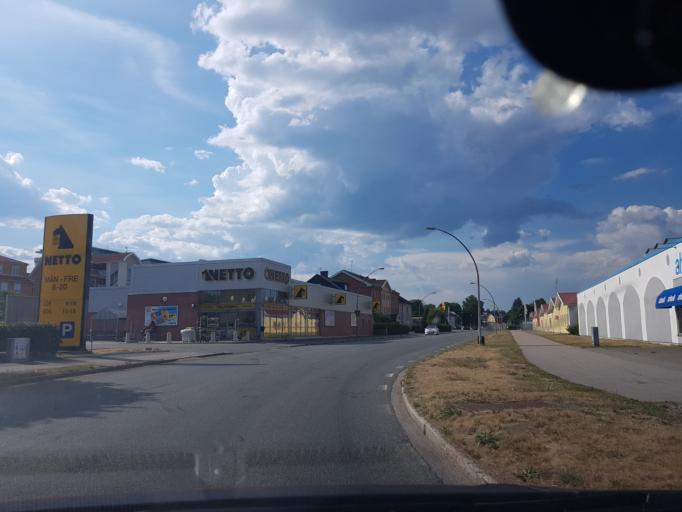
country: SE
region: Joenkoeping
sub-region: Gislaveds Kommun
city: Gislaved
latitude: 57.3019
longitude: 13.5445
